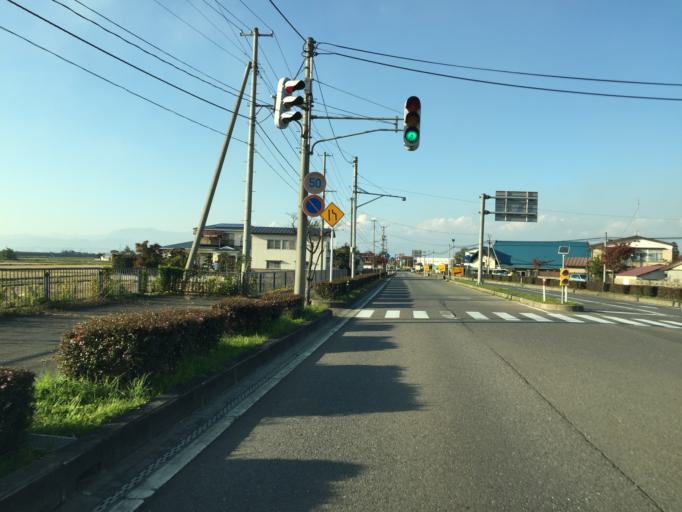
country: JP
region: Fukushima
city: Kitakata
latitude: 37.5373
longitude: 139.9145
